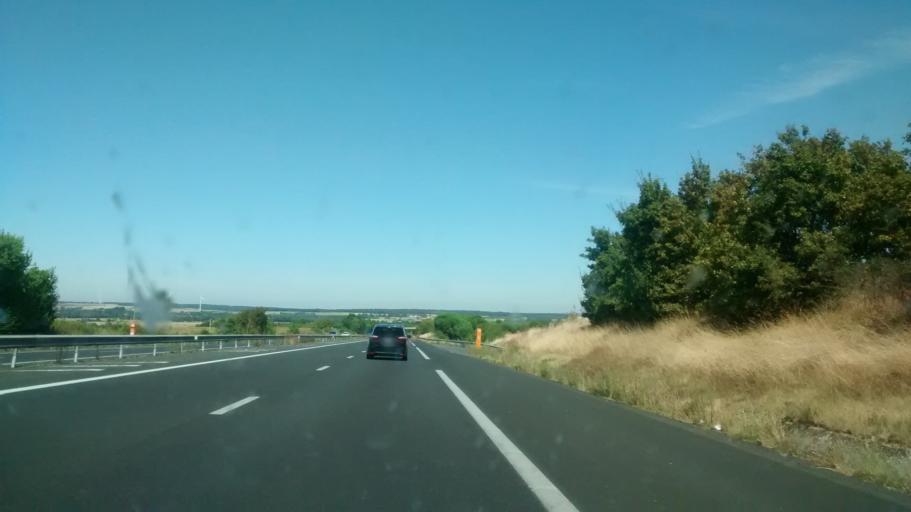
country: FR
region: Poitou-Charentes
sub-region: Departement de la Charente-Maritime
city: Saint-Jean-d'Angely
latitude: 46.0428
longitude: -0.5367
